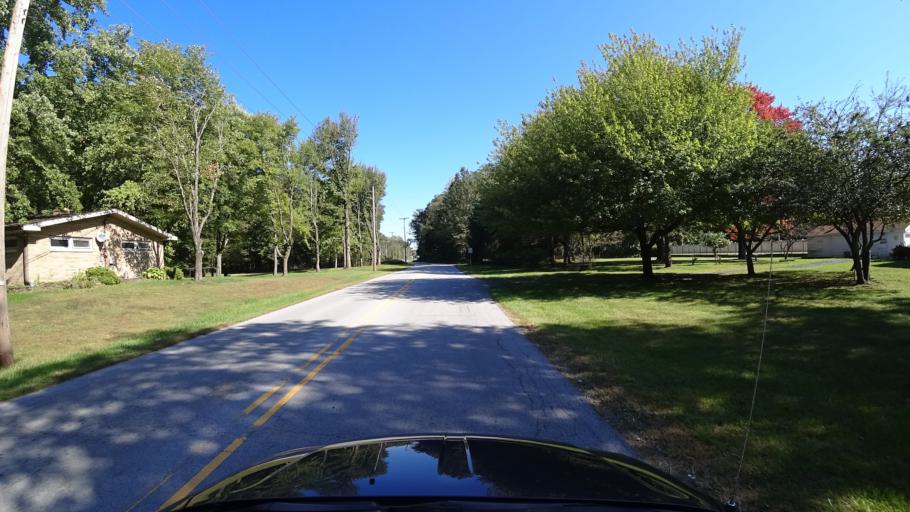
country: US
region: Indiana
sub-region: LaPorte County
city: Michigan City
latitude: 41.6837
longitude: -86.9035
